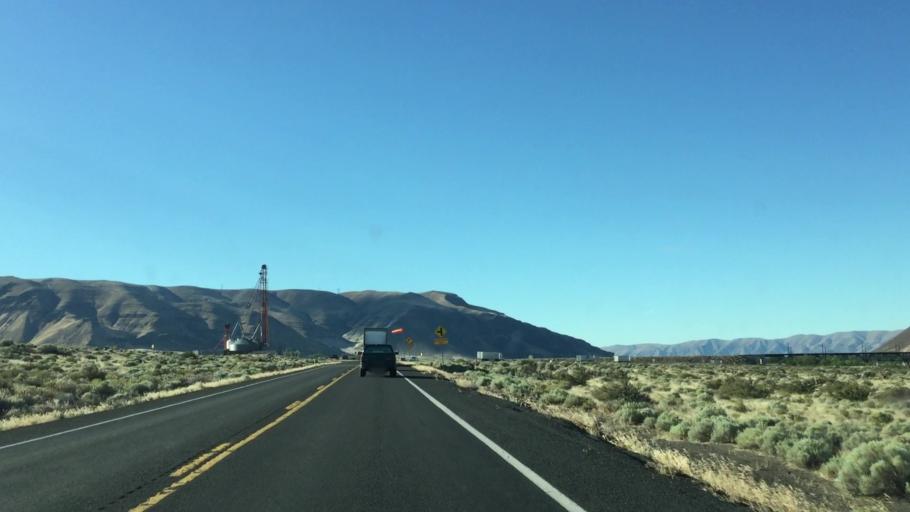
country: US
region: Washington
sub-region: Grant County
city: Mattawa
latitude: 46.8451
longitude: -119.9392
